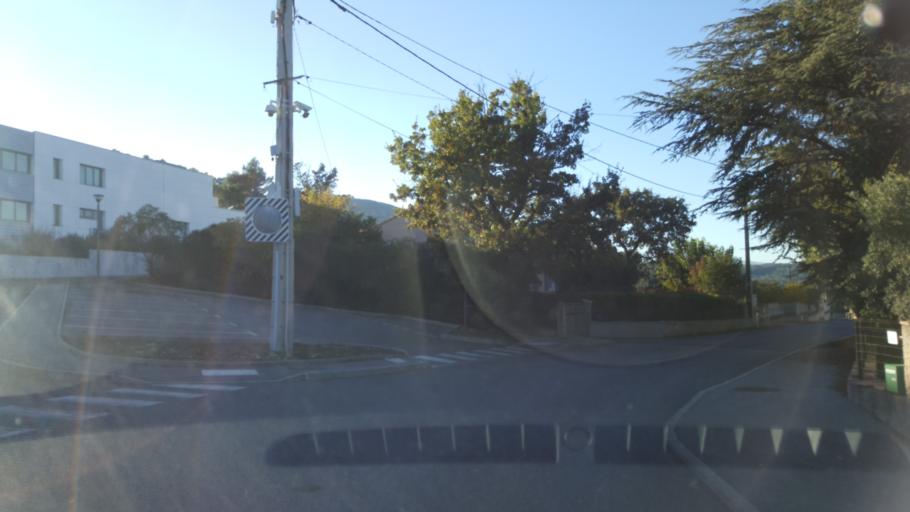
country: FR
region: Provence-Alpes-Cote d'Azur
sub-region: Departement du Var
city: Saint-Maximin-la-Sainte-Baume
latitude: 43.4508
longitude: 5.8529
